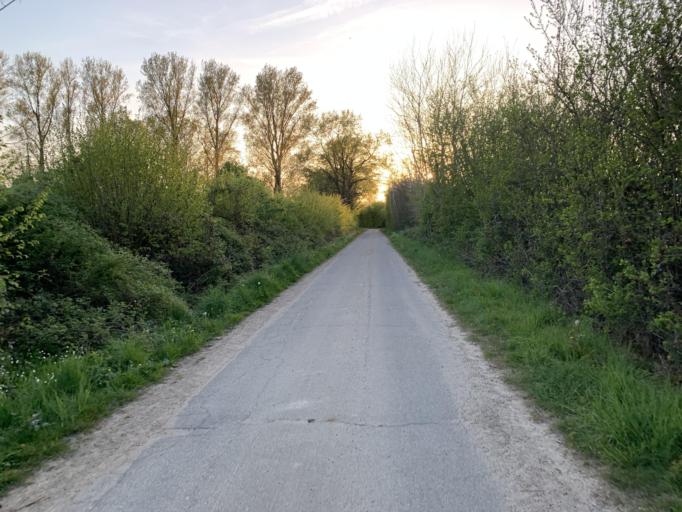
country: DE
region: Schleswig-Holstein
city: Worth
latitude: 53.4688
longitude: 10.4192
